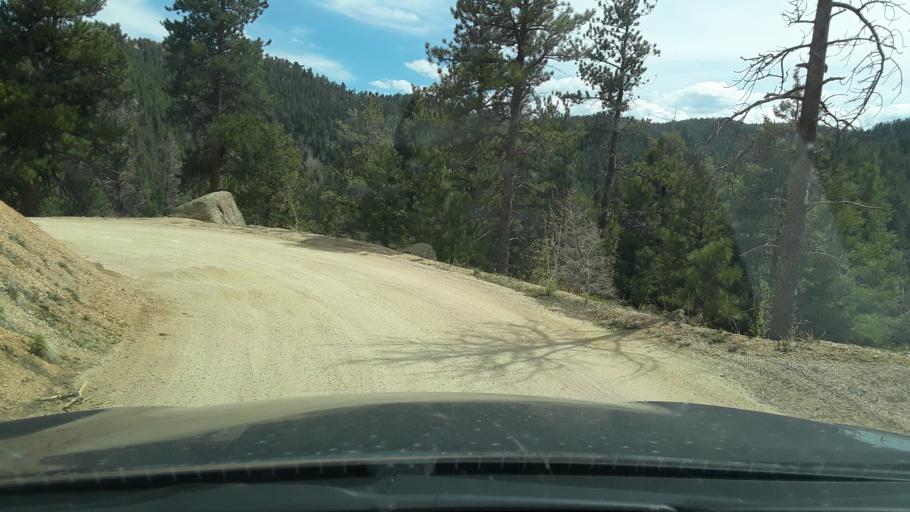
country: US
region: Colorado
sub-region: El Paso County
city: Palmer Lake
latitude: 39.0672
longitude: -104.9397
